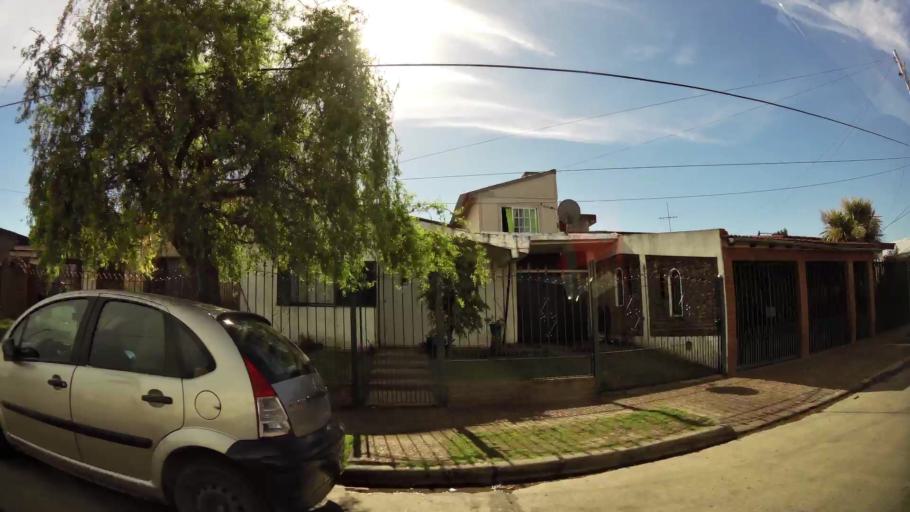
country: AR
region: Buenos Aires
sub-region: Partido de Almirante Brown
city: Adrogue
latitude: -34.8208
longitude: -58.3496
